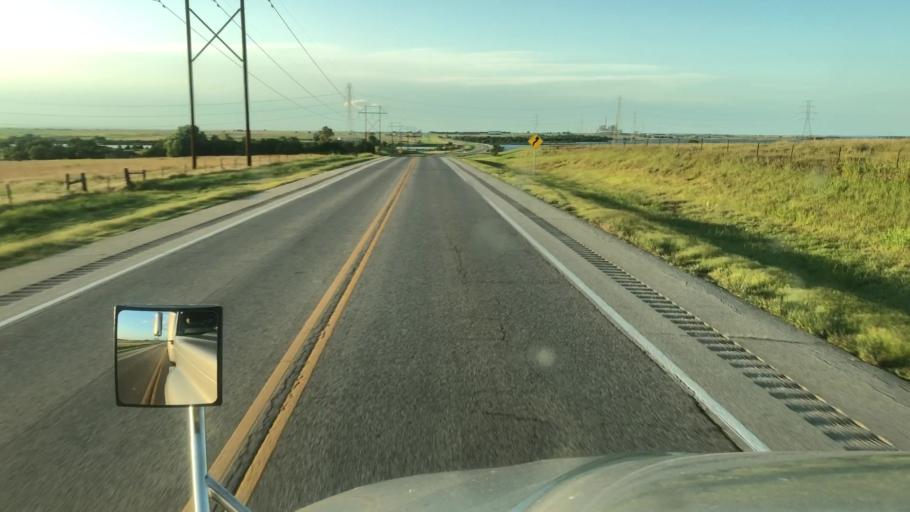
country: US
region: Oklahoma
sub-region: Noble County
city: Perry
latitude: 36.3967
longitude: -97.0676
